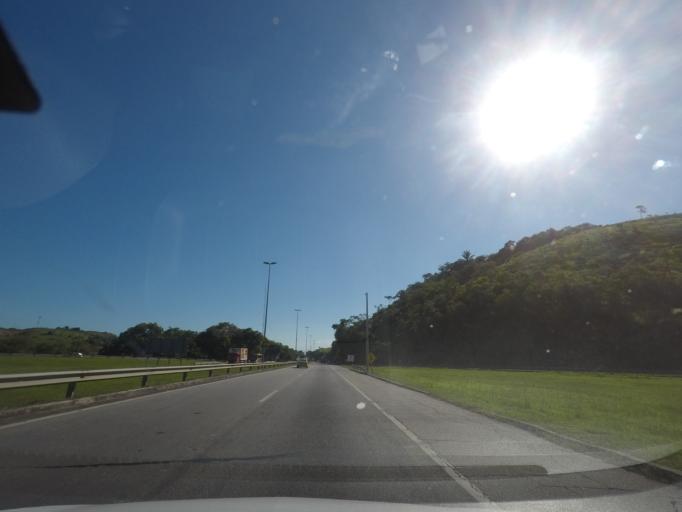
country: BR
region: Rio de Janeiro
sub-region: Guapimirim
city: Guapimirim
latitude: -22.6576
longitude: -43.0896
